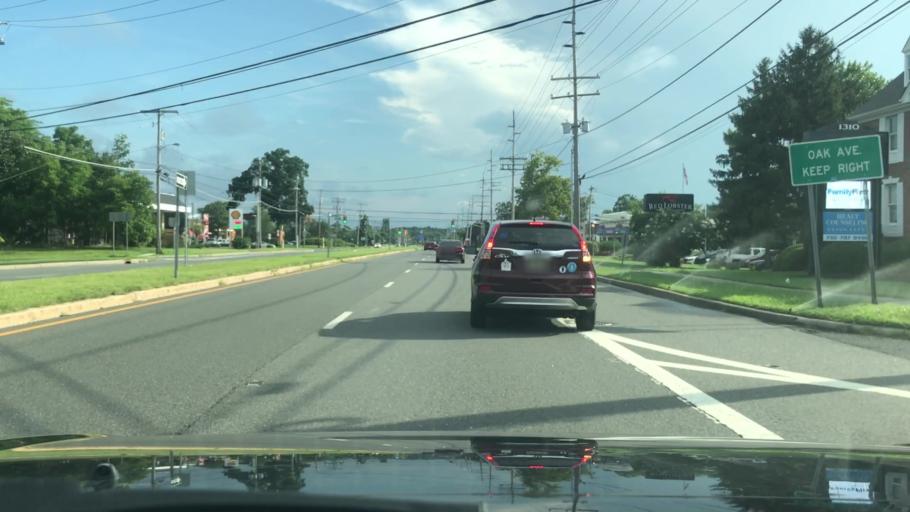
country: US
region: New Jersey
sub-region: Ocean County
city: Toms River
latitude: 39.9874
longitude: -74.1781
